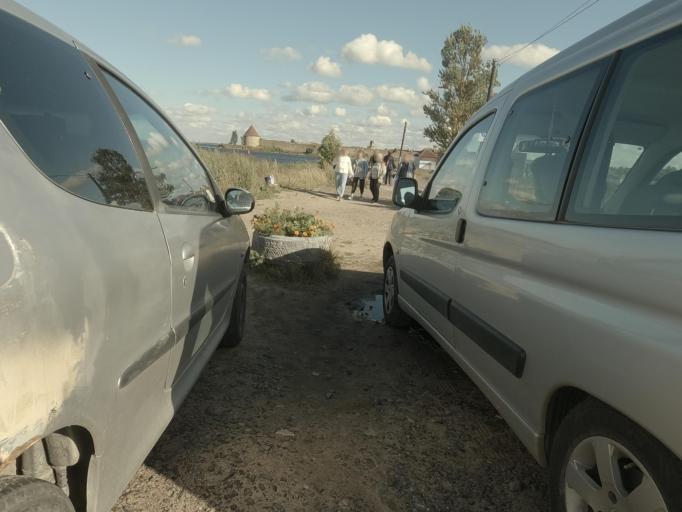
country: RU
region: Leningrad
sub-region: Volosovskiy Rayon
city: Shlissel'burg
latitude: 59.9580
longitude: 31.0317
